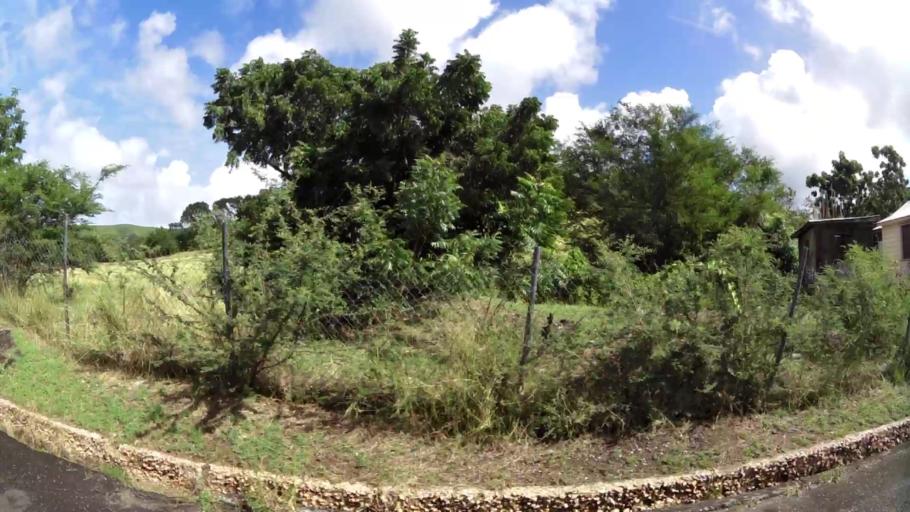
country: AG
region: Saint Mary
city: Bolands
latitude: 17.0676
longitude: -61.8741
